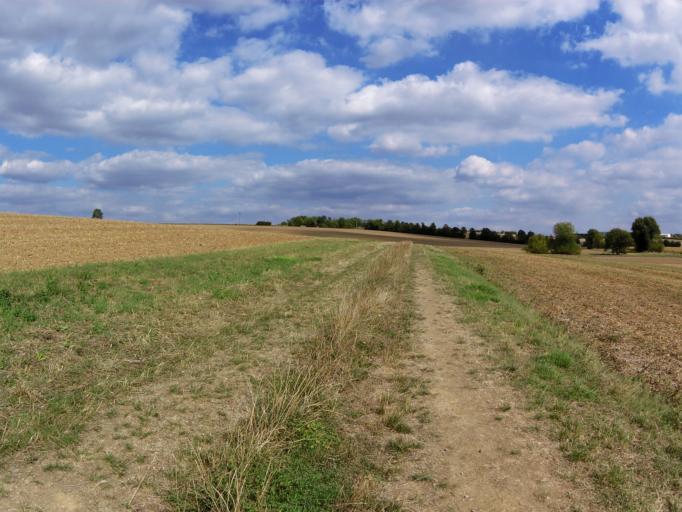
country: DE
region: Bavaria
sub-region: Regierungsbezirk Unterfranken
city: Hettstadt
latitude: 49.7926
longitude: 9.8278
